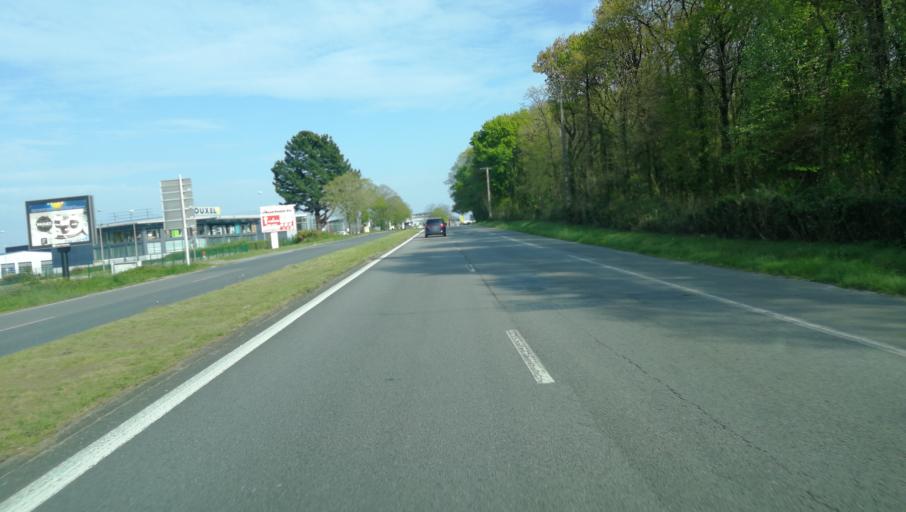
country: FR
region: Pays de la Loire
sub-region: Departement de la Loire-Atlantique
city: Orvault
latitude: 47.2559
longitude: -1.6349
